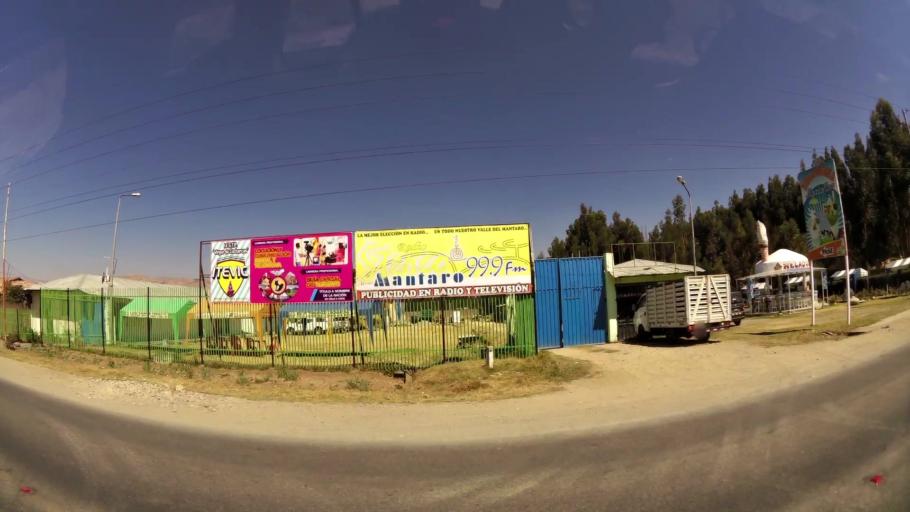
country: PE
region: Junin
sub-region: Provincia de Jauja
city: San Lorenzo
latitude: -11.8671
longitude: -75.3722
